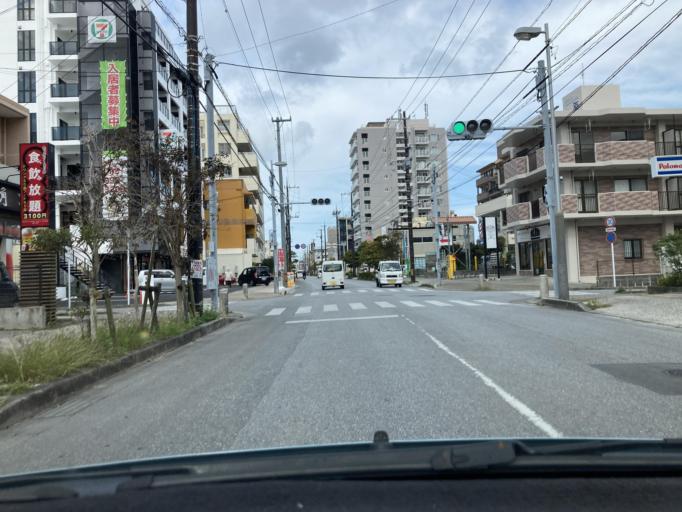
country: JP
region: Okinawa
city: Naha-shi
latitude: 26.2336
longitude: 127.6930
